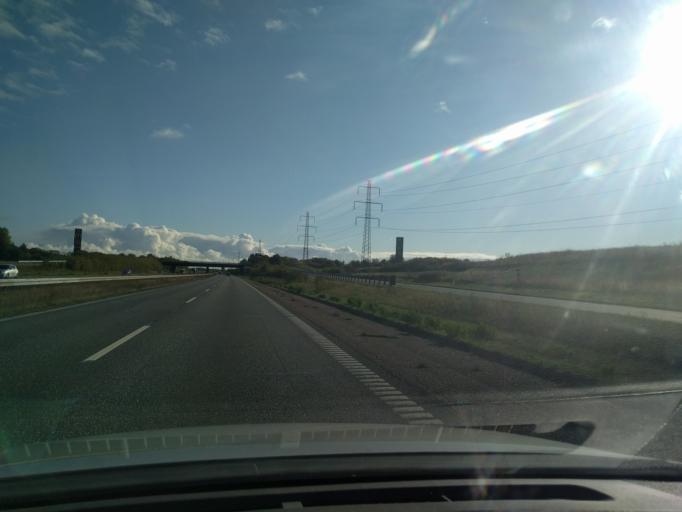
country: DK
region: Zealand
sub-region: Ringsted Kommune
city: Ringsted
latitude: 55.4548
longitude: 11.7846
